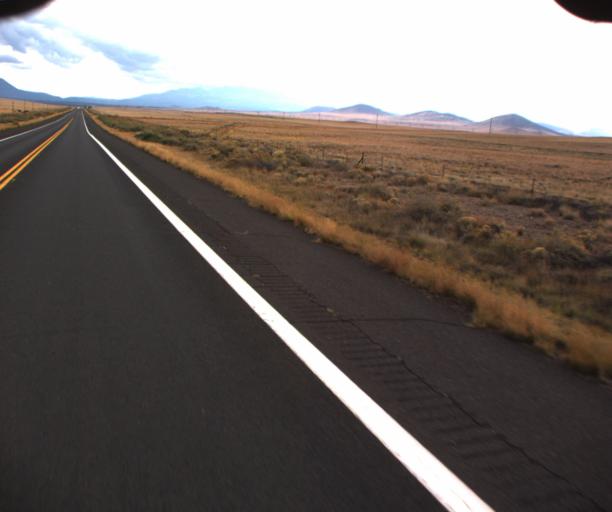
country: US
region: Arizona
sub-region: Coconino County
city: Flagstaff
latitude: 35.6211
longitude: -111.5219
